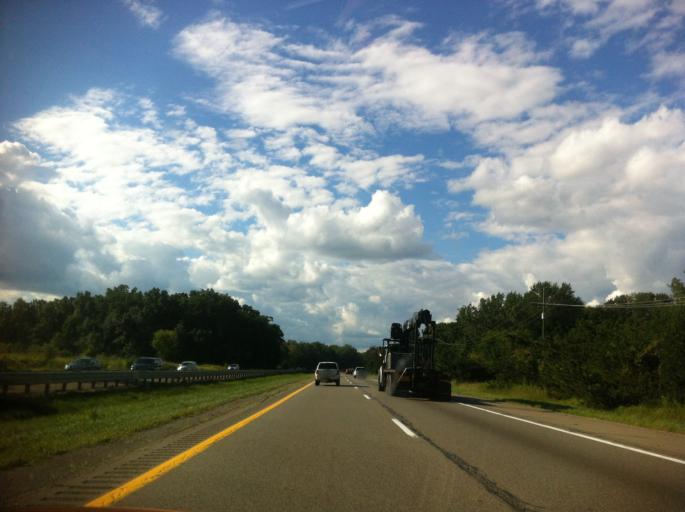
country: US
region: Michigan
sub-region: Livingston County
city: Whitmore Lake
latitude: 42.3838
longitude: -83.7595
